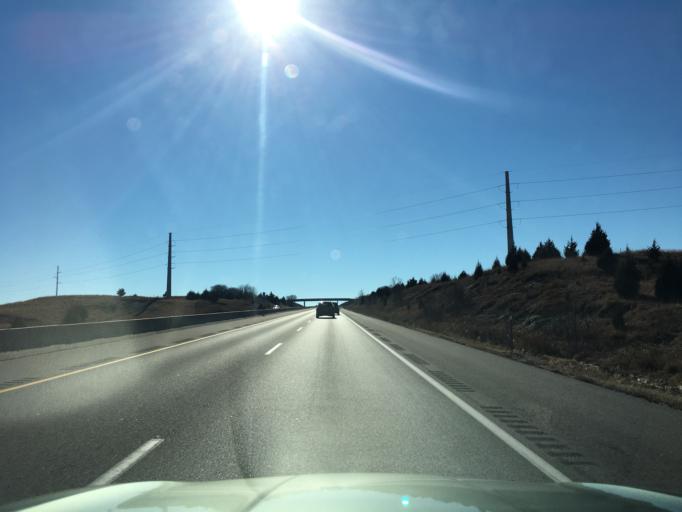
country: US
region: Kansas
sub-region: Sumner County
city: Wellington
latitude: 37.2077
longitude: -97.3401
